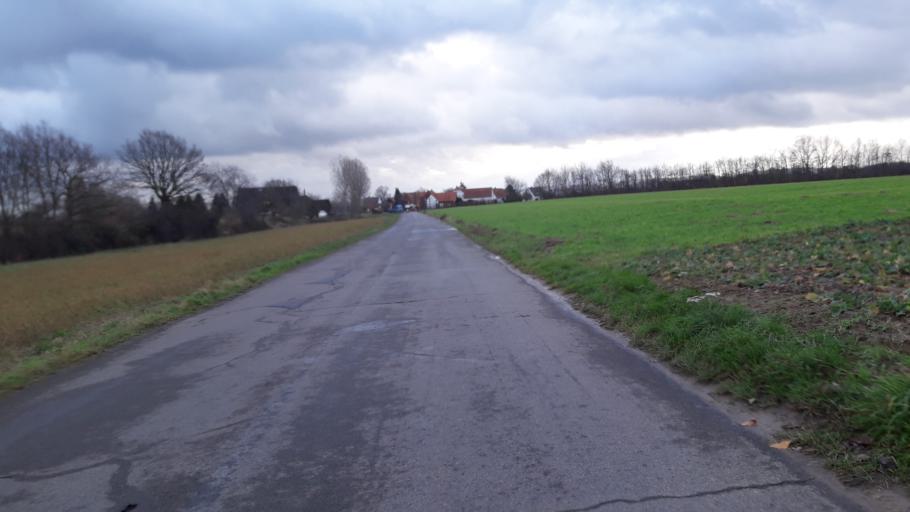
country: DE
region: North Rhine-Westphalia
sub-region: Regierungsbezirk Detmold
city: Petershagen
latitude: 52.3299
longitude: 8.9656
